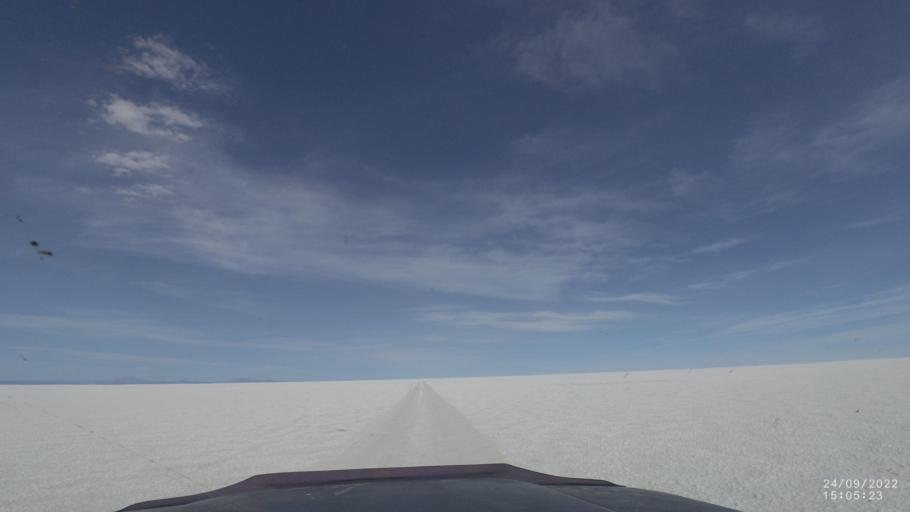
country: BO
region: Potosi
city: Colchani
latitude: -19.9058
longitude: -67.5178
